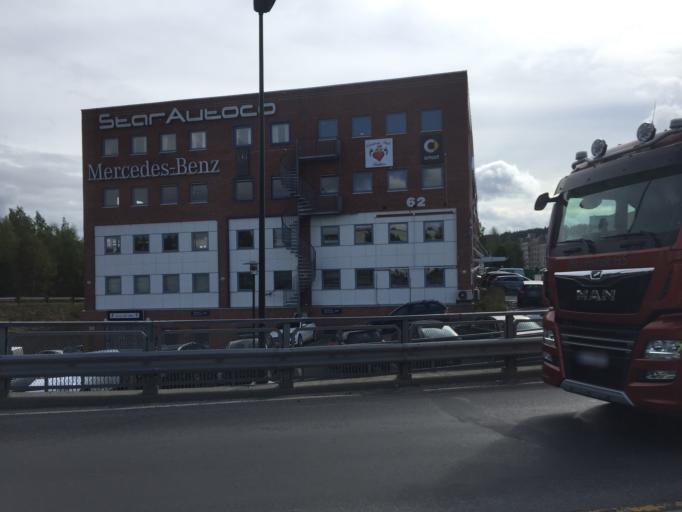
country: NO
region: Akershus
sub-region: Lorenskog
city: Kjenn
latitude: 59.9297
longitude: 10.9467
